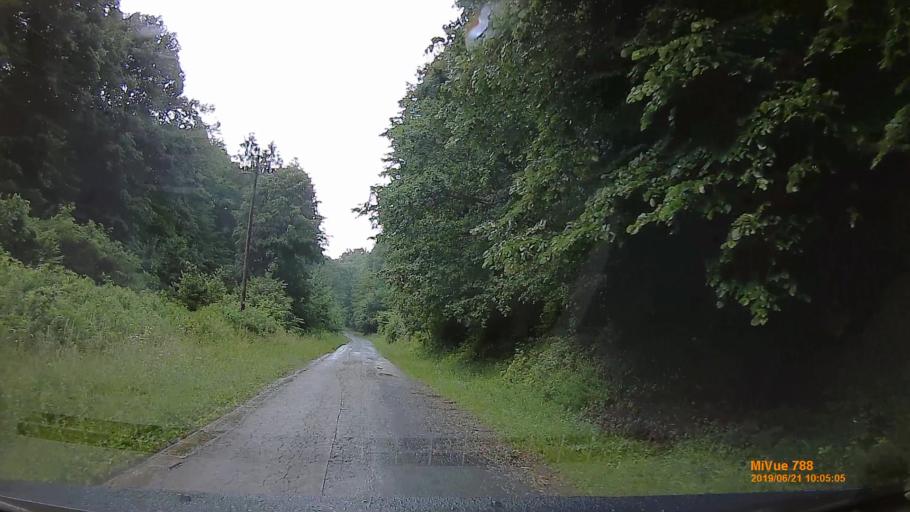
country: HU
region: Baranya
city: Buekkoesd
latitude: 46.1994
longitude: 17.9621
